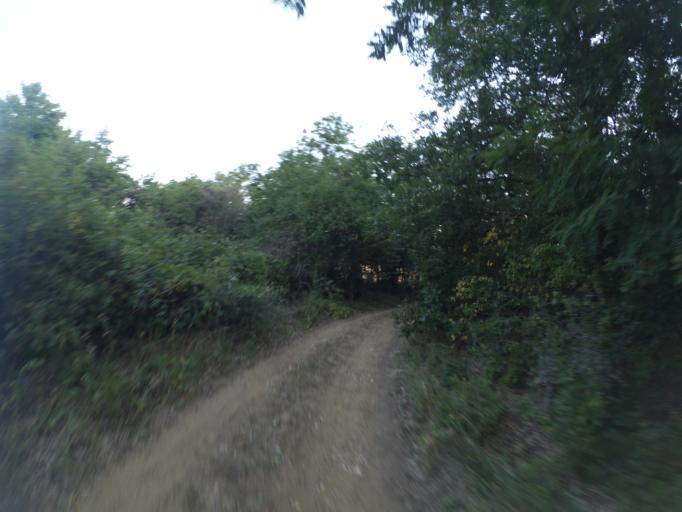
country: HU
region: Pest
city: Pilisszanto
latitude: 47.6689
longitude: 18.8707
